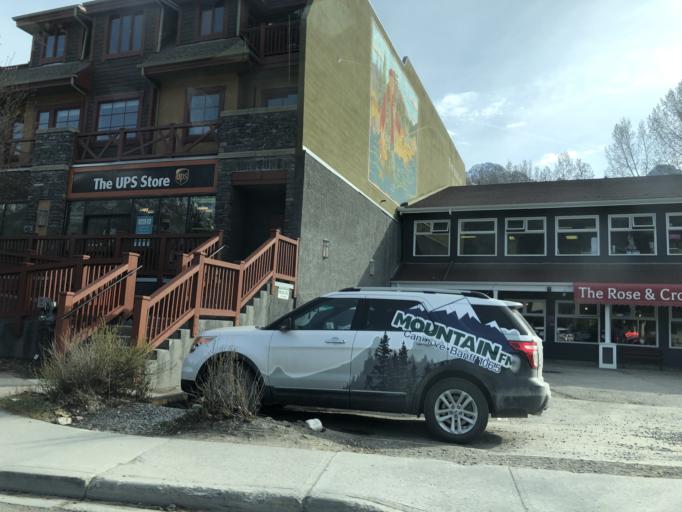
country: CA
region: Alberta
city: Canmore
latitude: 51.0895
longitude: -115.3538
